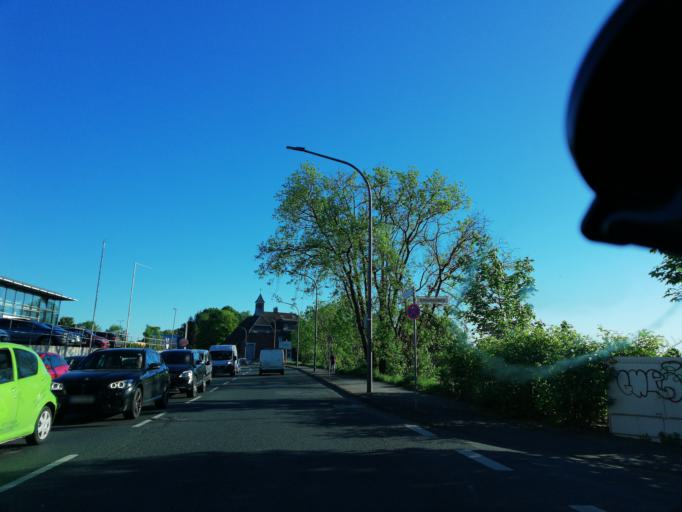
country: DE
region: North Rhine-Westphalia
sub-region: Regierungsbezirk Dusseldorf
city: Wuppertal
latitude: 51.2472
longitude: 7.1924
